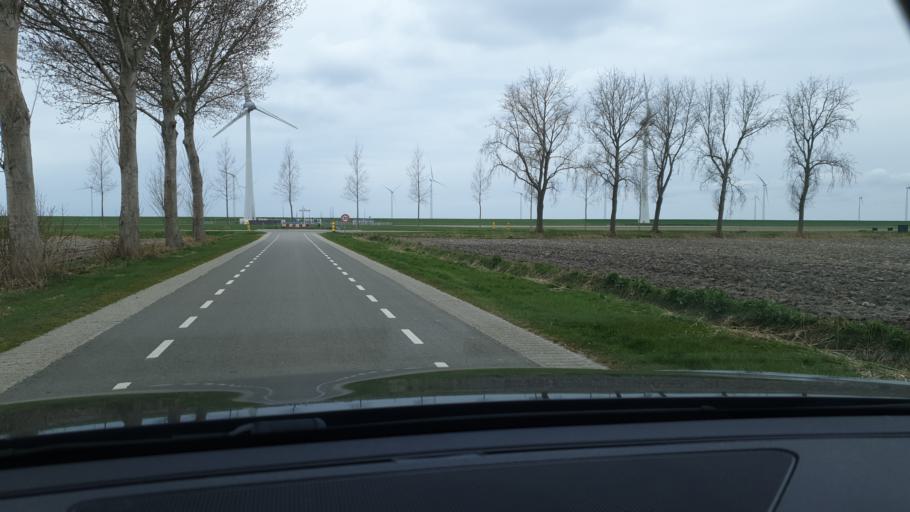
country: NL
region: Flevoland
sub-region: Gemeente Urk
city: Urk
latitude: 52.7254
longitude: 5.6094
